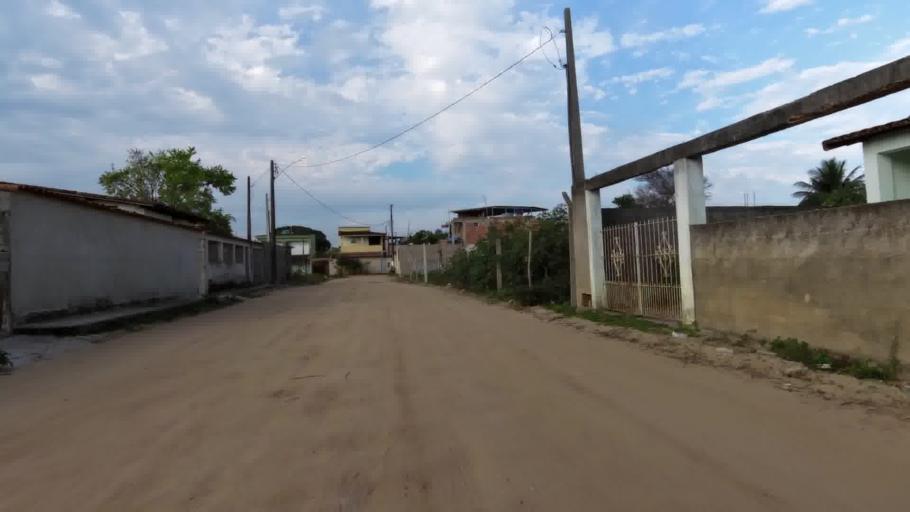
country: BR
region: Espirito Santo
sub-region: Piuma
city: Piuma
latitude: -20.8413
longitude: -40.7480
